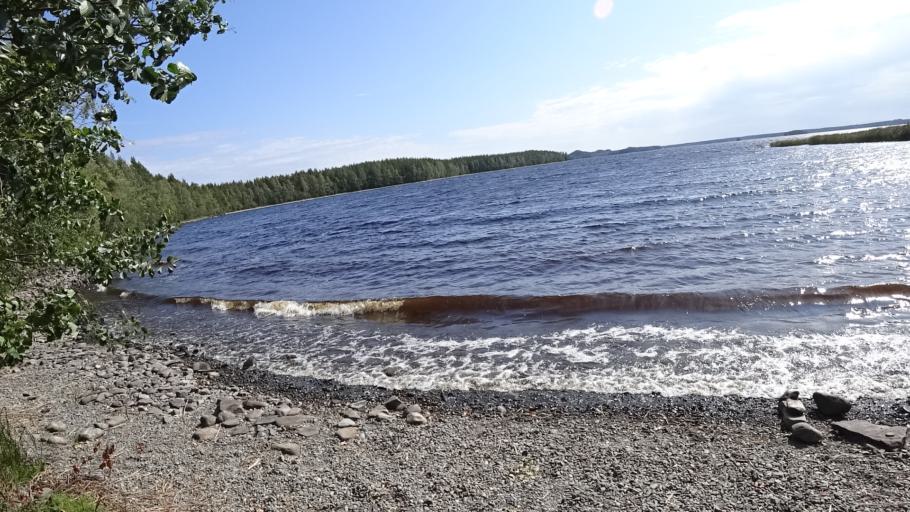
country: FI
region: North Karelia
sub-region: Keski-Karjala
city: Raeaekkylae
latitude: 62.3948
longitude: 29.7597
